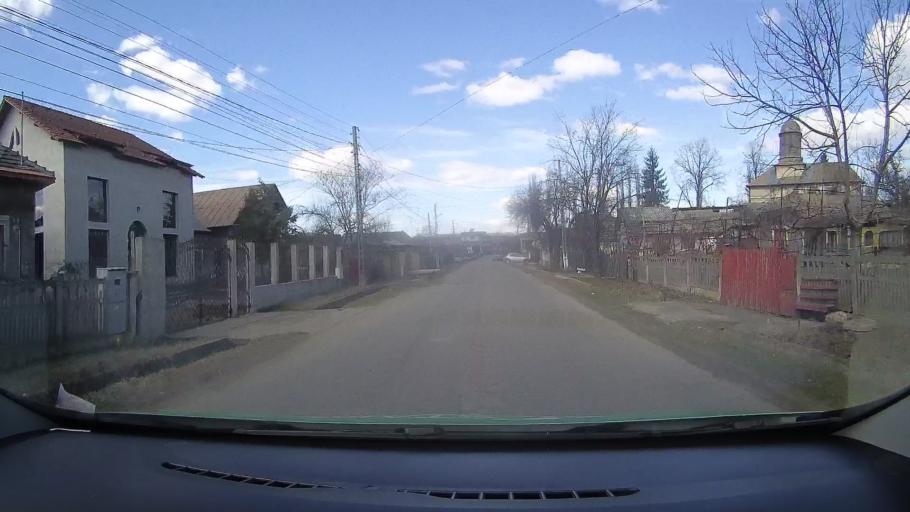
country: RO
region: Dambovita
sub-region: Comuna Doicesti
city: Doicesti
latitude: 44.9923
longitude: 25.3932
